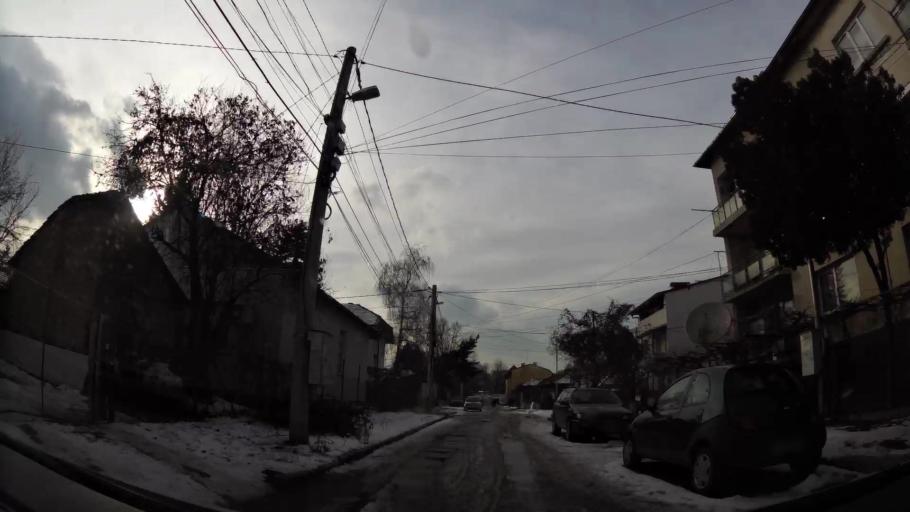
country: BG
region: Sofia-Capital
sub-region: Stolichna Obshtina
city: Sofia
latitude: 42.6995
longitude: 23.3771
